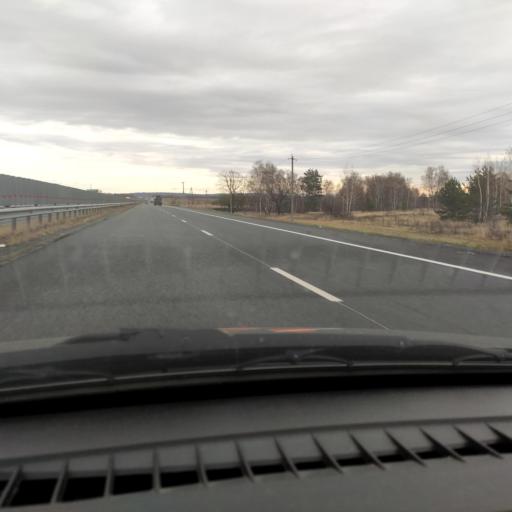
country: RU
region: Samara
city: Bogatyr'
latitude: 53.5095
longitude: 49.9567
